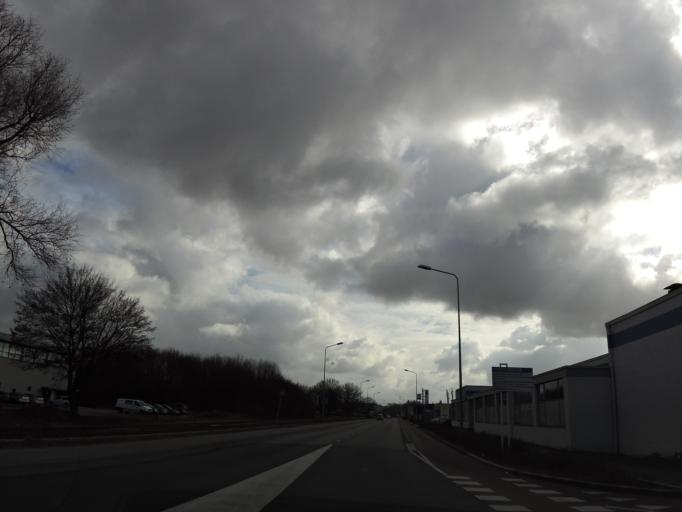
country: NL
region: Limburg
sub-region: Gemeente Maastricht
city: Maastricht
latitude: 50.8744
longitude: 5.7096
